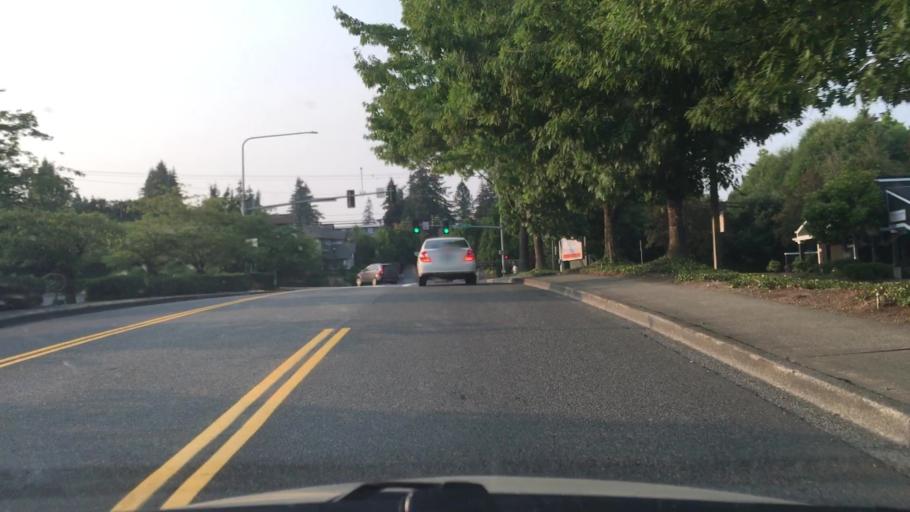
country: US
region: Washington
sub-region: King County
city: Kingsgate
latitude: 47.7178
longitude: -122.1809
